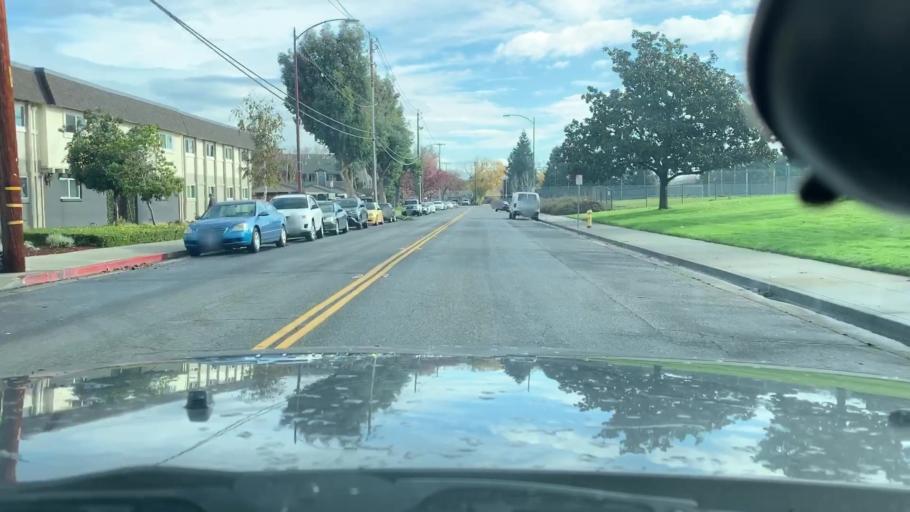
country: US
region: California
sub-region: Santa Clara County
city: Campbell
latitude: 37.3143
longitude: -121.9685
